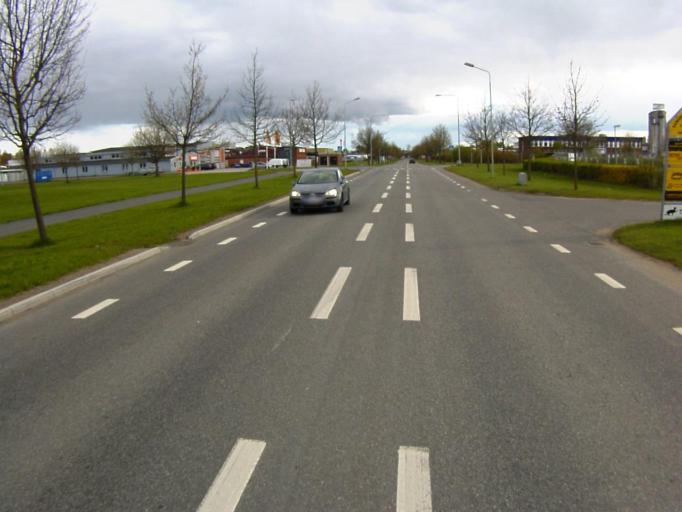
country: SE
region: Skane
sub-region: Kristianstads Kommun
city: Kristianstad
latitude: 56.0498
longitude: 14.1625
